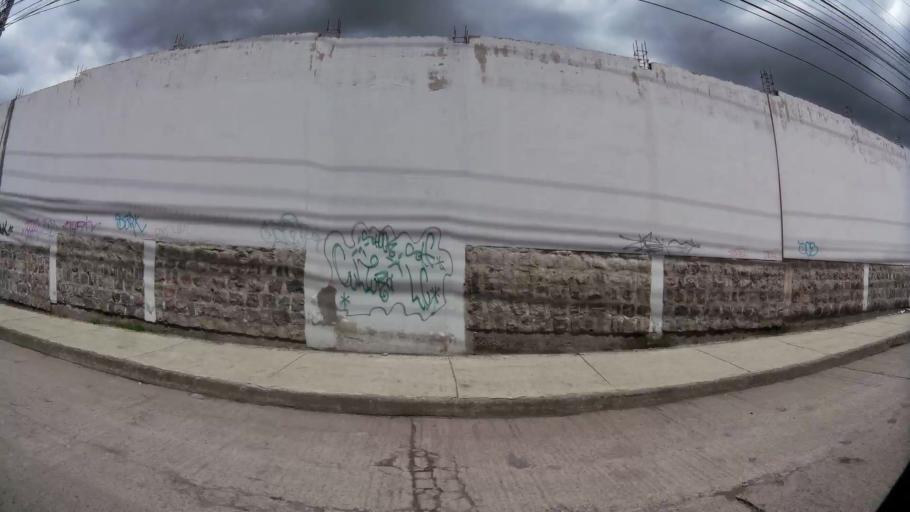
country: EC
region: Pichincha
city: Sangolqui
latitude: -0.3466
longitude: -78.5457
